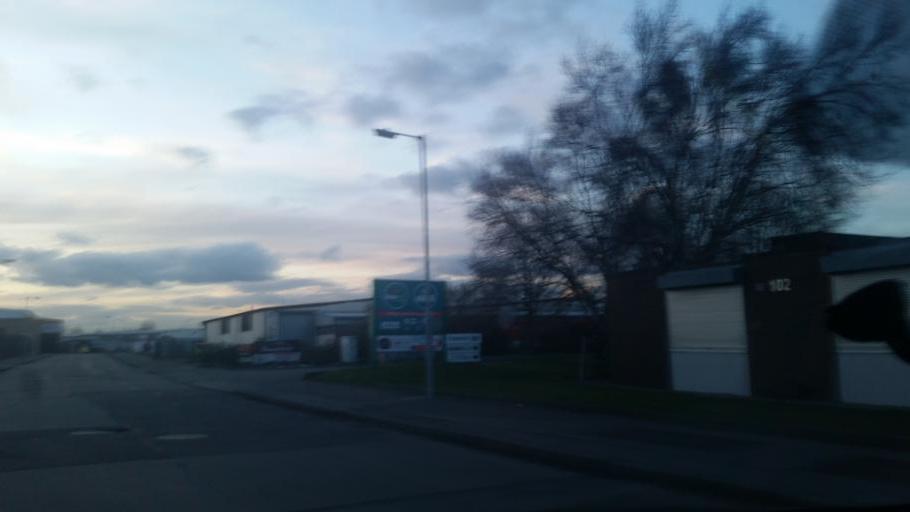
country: IE
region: Leinster
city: Cabra
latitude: 53.3738
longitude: -6.2902
